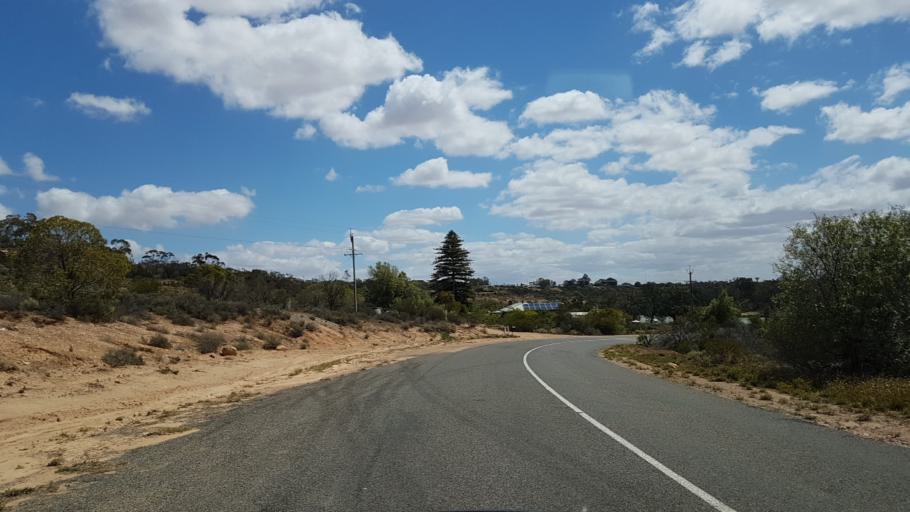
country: AU
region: South Australia
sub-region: Loxton Waikerie
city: Waikerie
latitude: -34.1847
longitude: 140.0166
